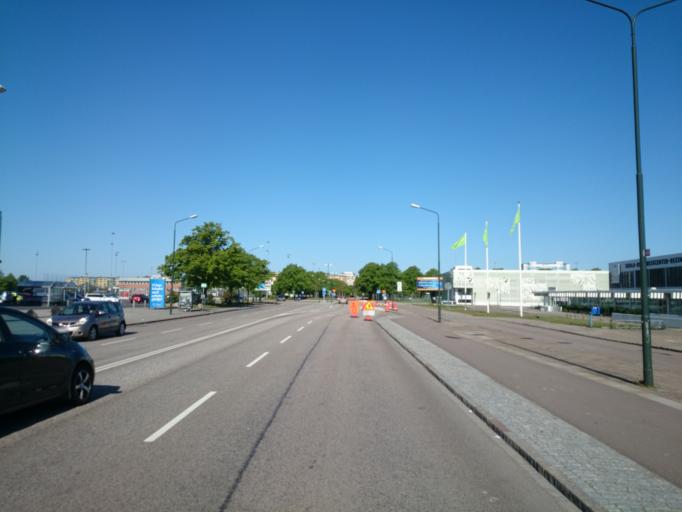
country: SE
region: Skane
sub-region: Malmo
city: Malmoe
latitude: 55.5809
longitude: 12.9911
